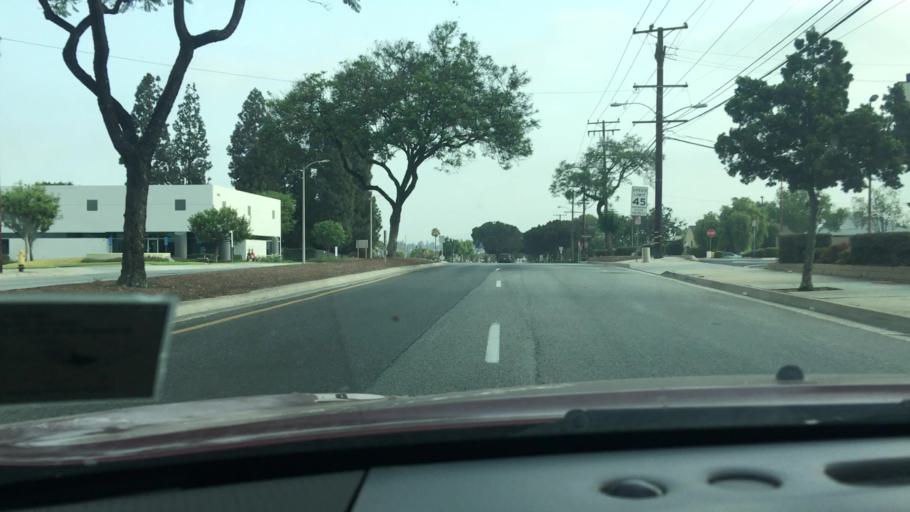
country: US
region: California
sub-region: Los Angeles County
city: La Mirada
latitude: 33.9033
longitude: -118.0291
